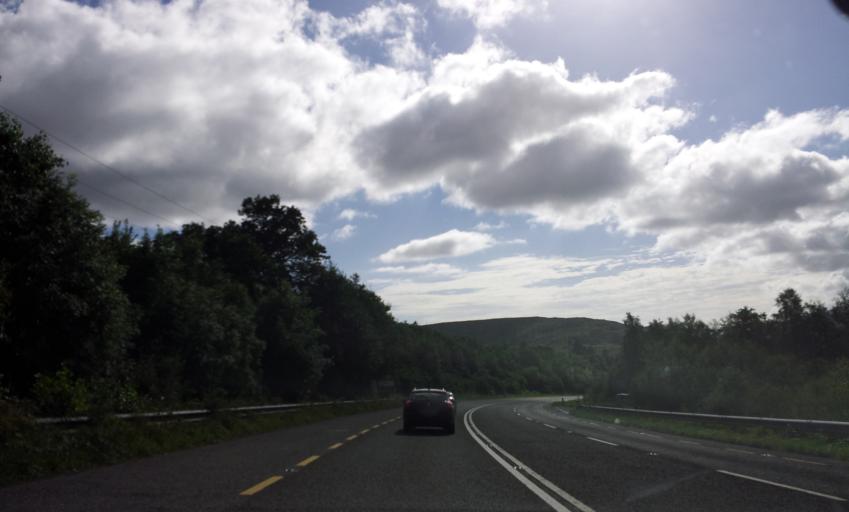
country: IE
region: Munster
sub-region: Ciarrai
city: Cill Airne
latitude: 51.9839
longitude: -9.3014
